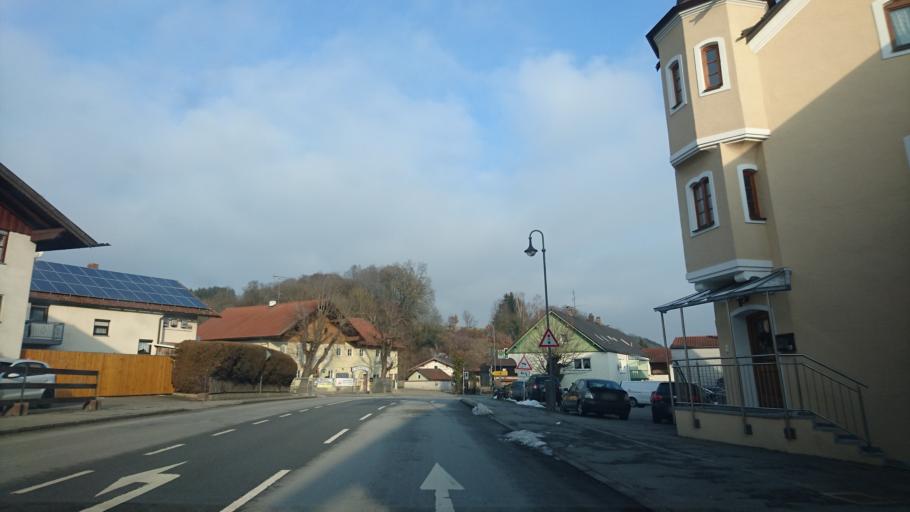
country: DE
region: Bavaria
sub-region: Lower Bavaria
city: Triftern
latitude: 48.4432
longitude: 13.0138
